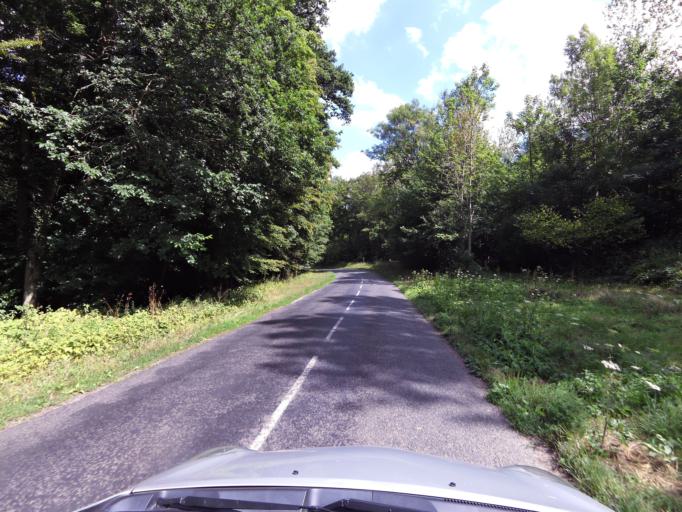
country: FR
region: Picardie
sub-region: Departement de l'Aisne
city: La Ferte-Milon
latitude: 49.2510
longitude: 3.1917
